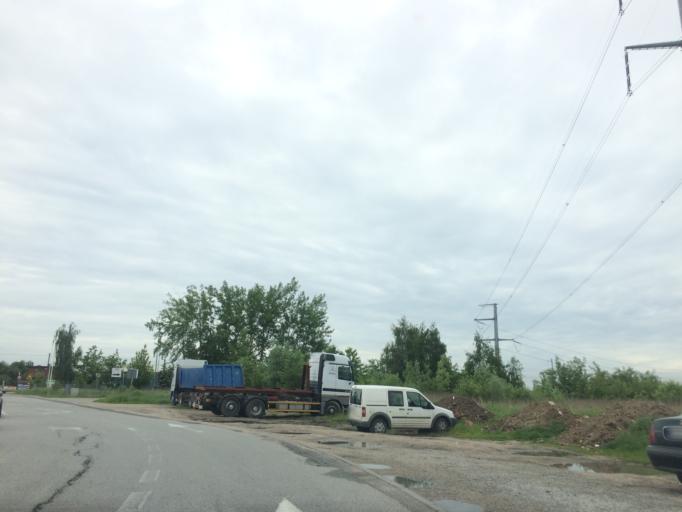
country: PL
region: Lower Silesian Voivodeship
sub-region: Powiat wroclawski
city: Dlugoleka
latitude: 51.1745
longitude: 17.1792
